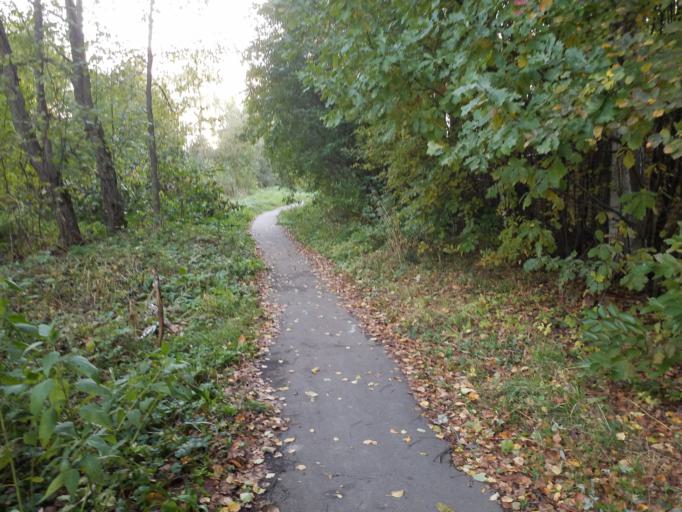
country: RU
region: Moskovskaya
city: Ashukino
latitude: 56.1591
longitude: 37.9561
